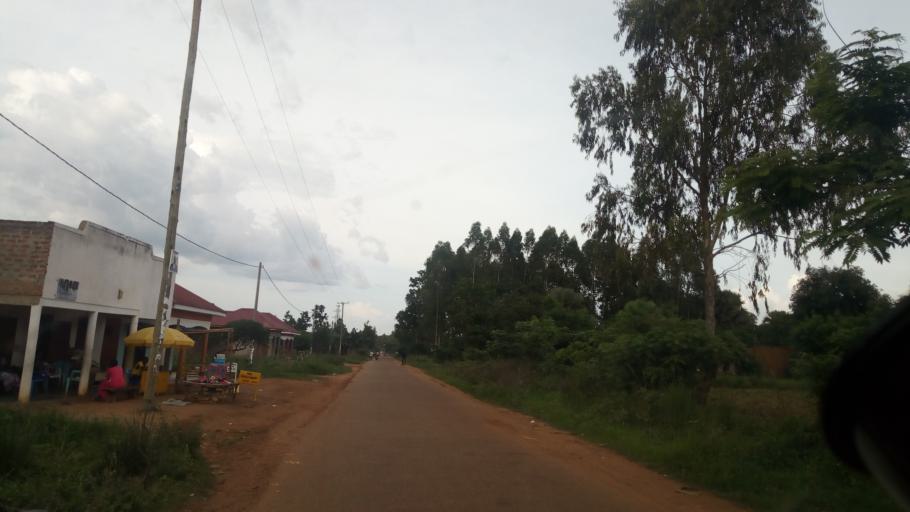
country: UG
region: Northern Region
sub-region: Lira District
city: Lira
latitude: 2.2617
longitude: 32.8600
